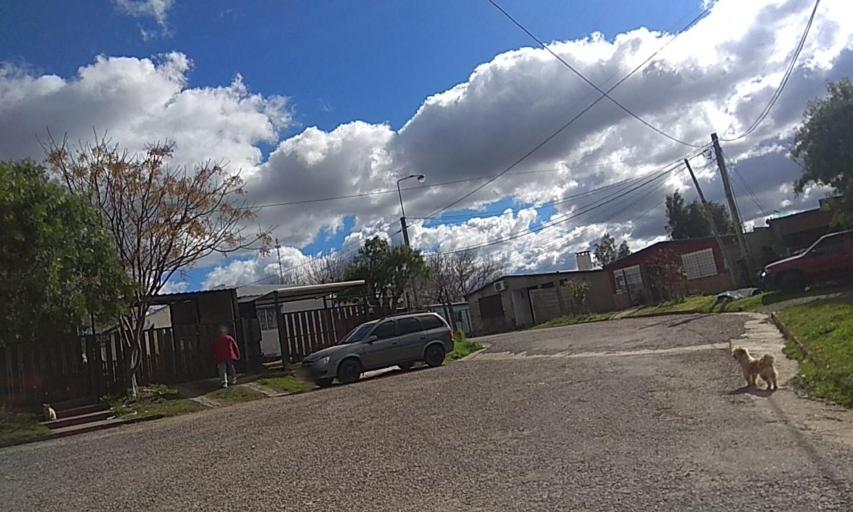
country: UY
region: Florida
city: Florida
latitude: -34.0890
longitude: -56.2282
